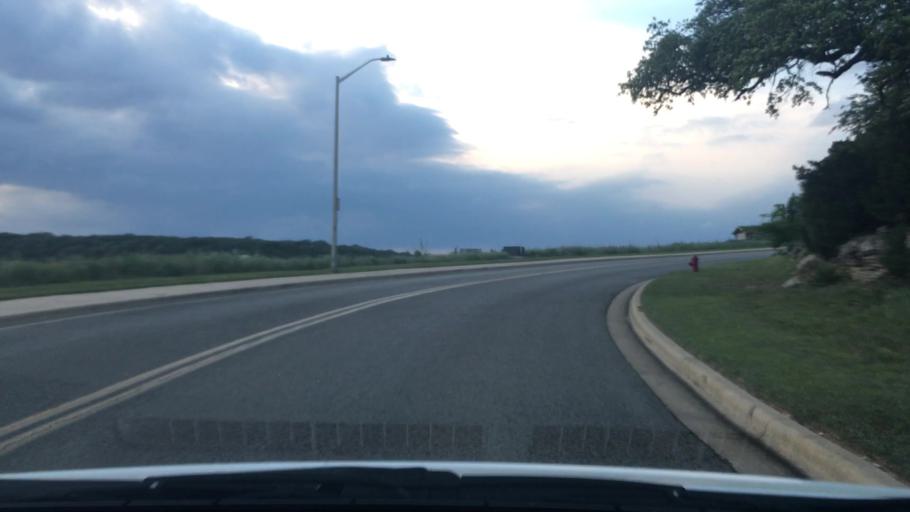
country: US
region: Texas
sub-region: Williamson County
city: Anderson Mill
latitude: 30.4525
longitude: -97.8592
